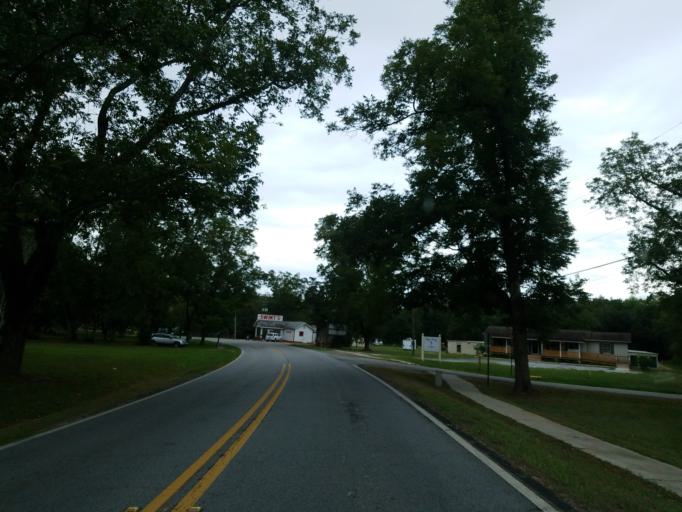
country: US
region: Georgia
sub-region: Lamar County
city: Barnesville
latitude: 33.1107
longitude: -84.1958
